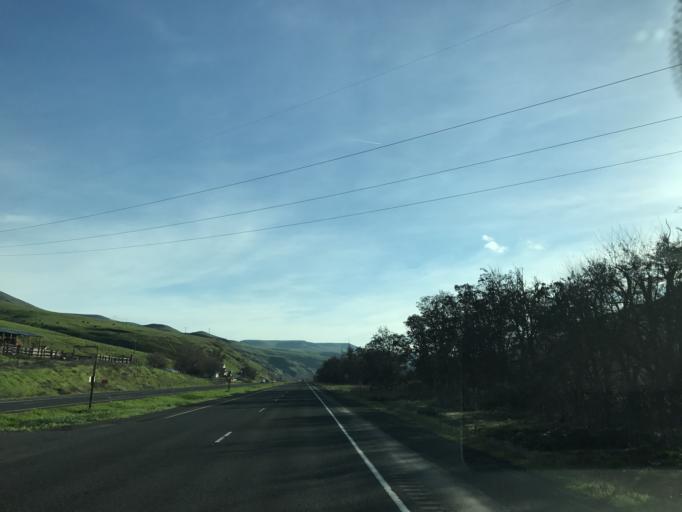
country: US
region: Idaho
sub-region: Nez Perce County
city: Lewiston Orchards
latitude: 46.4376
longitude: -116.9023
